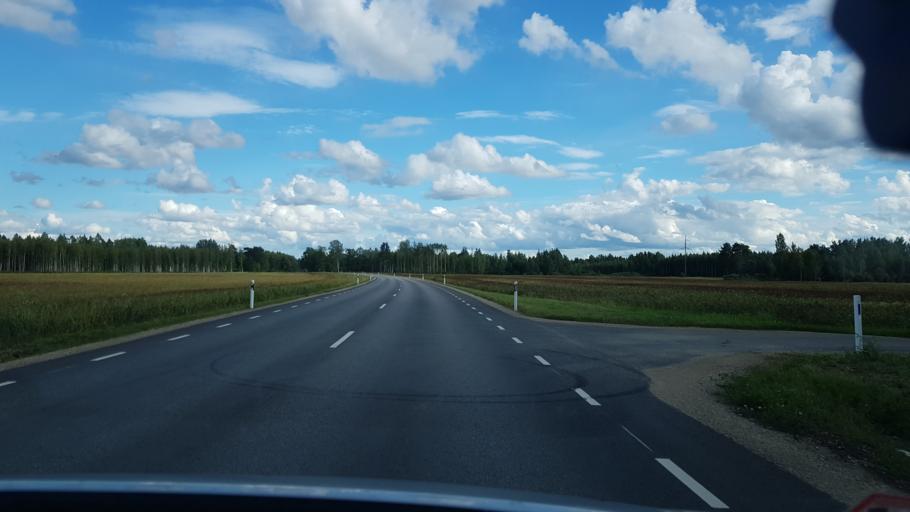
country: EE
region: Polvamaa
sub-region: Polva linn
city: Polva
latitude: 58.0804
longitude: 27.2406
